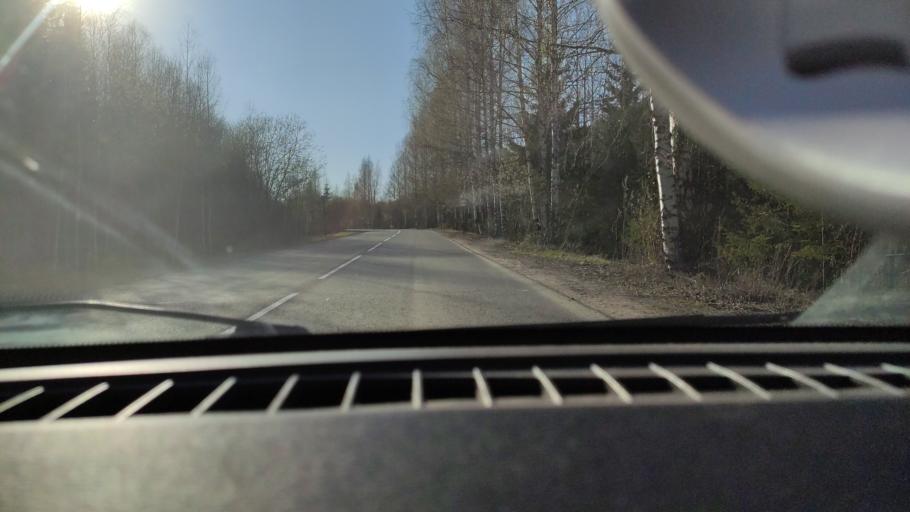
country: RU
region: Perm
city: Polazna
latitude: 58.1231
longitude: 56.4424
